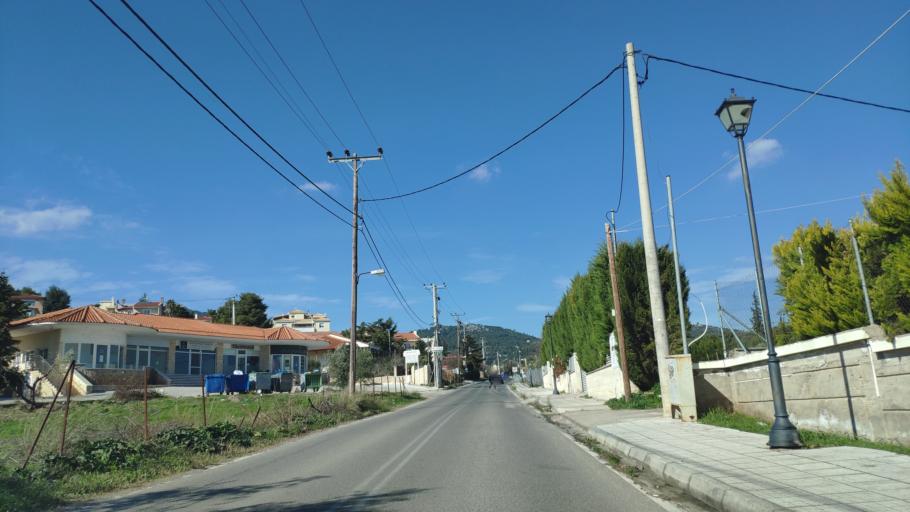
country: GR
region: Attica
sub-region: Nomarchia Anatolikis Attikis
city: Afidnes
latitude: 38.1963
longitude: 23.8427
